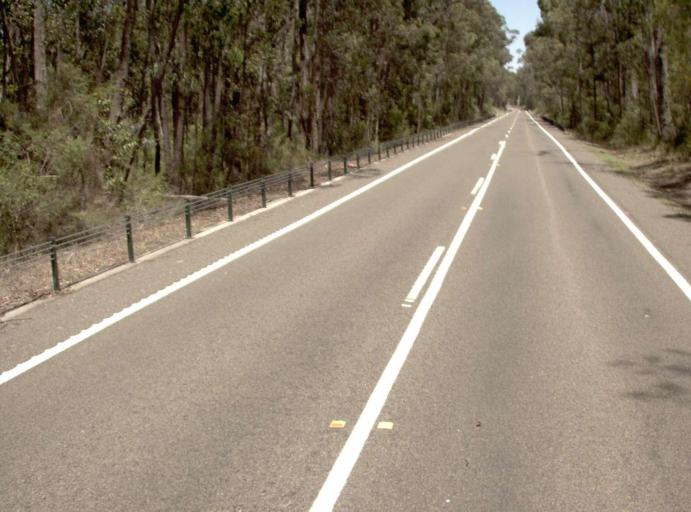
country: AU
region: Victoria
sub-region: East Gippsland
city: Lakes Entrance
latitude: -37.7596
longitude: 148.0609
